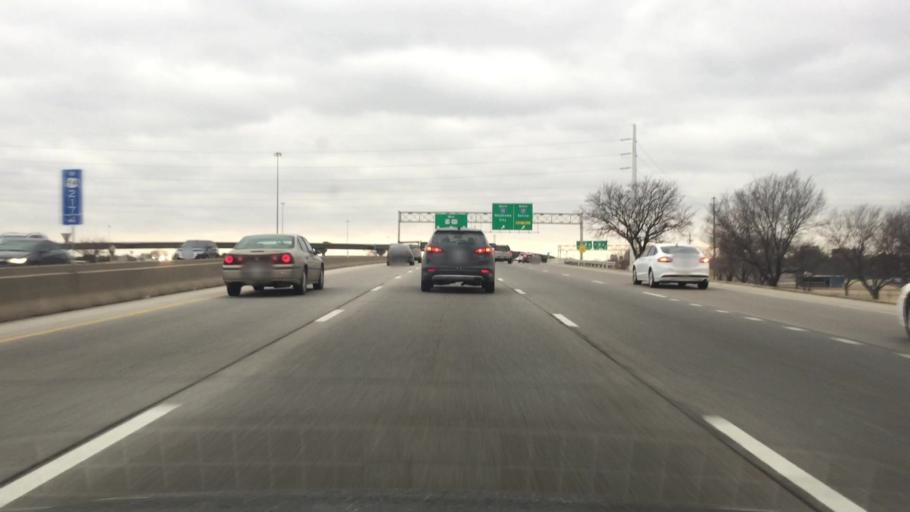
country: US
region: Kansas
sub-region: Sedgwick County
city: Wichita
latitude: 37.6783
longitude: -97.3077
